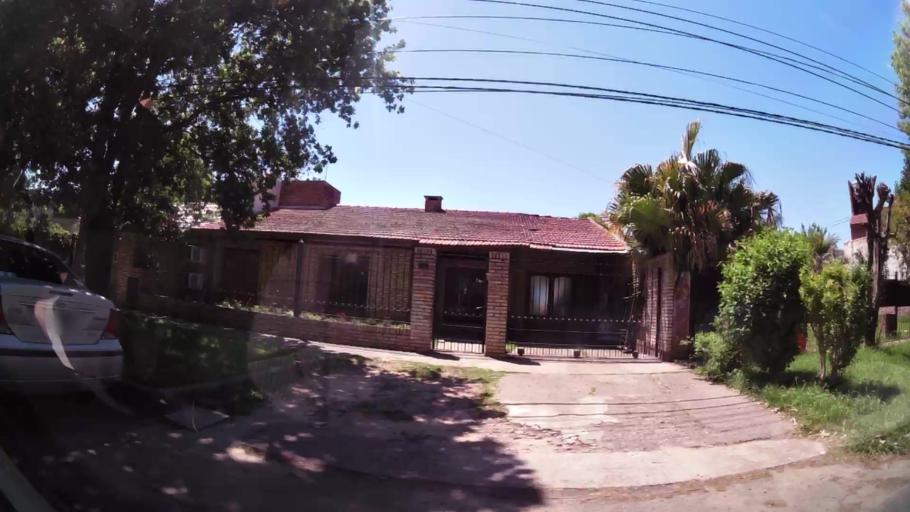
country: AR
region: Buenos Aires
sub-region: Partido de Tigre
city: Tigre
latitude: -34.4895
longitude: -58.6424
